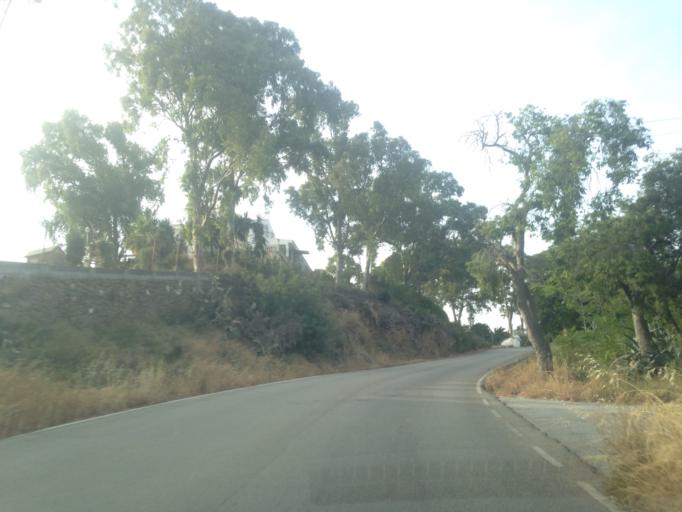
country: ES
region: Andalusia
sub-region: Provincia de Malaga
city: Malaga
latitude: 36.7445
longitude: -4.4110
